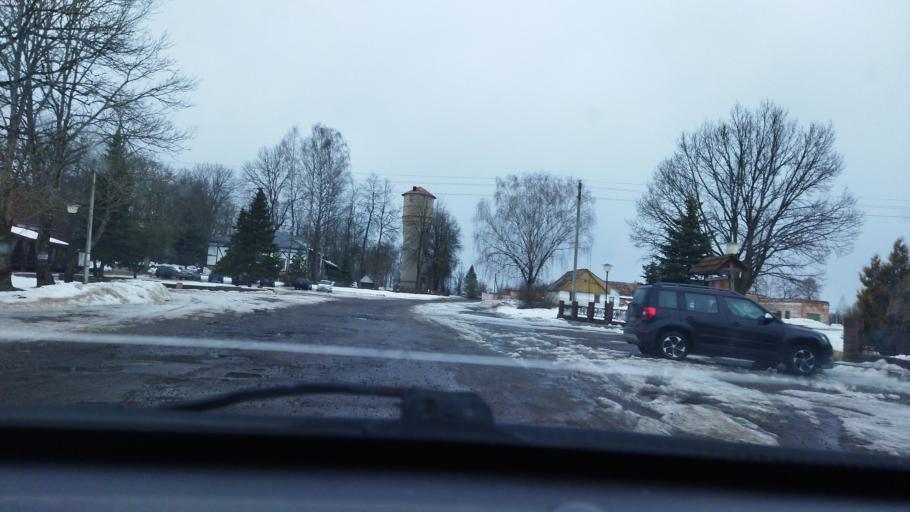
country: BY
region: Minsk
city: Svir
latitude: 54.9013
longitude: 26.4004
